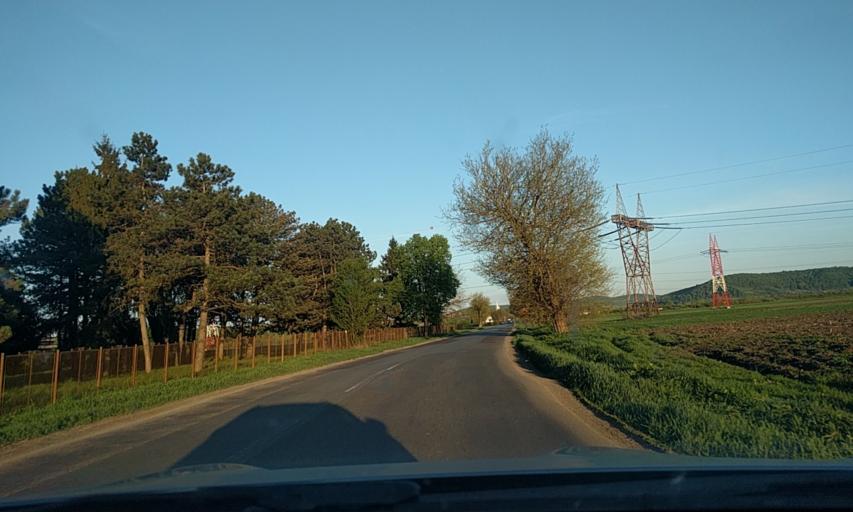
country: RO
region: Mures
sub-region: Comuna Ungheni
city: Ungheni
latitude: 46.4757
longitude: 24.4724
